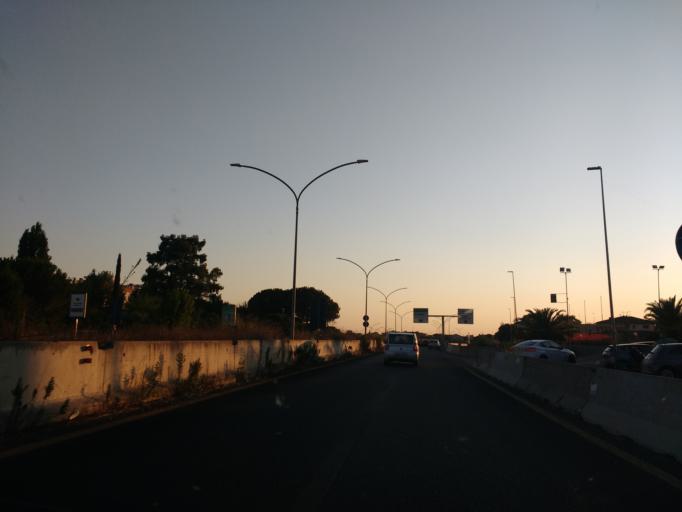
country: IT
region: Latium
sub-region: Citta metropolitana di Roma Capitale
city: Setteville
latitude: 41.9389
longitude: 12.6282
